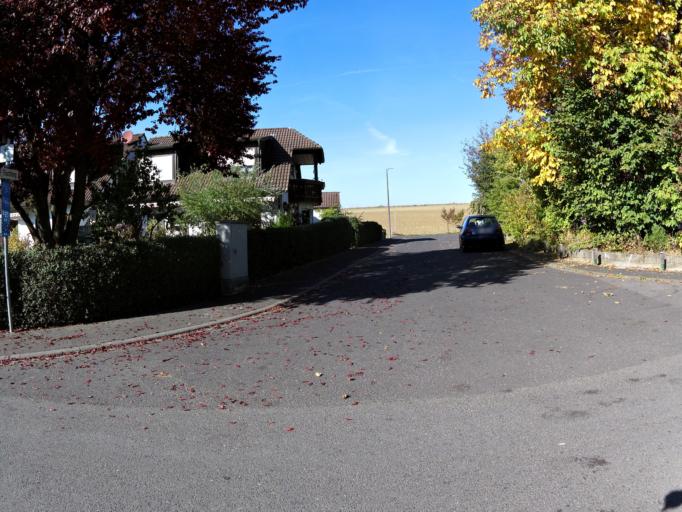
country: DE
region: Bavaria
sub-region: Regierungsbezirk Unterfranken
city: Reichenberg
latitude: 49.7116
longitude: 9.9331
